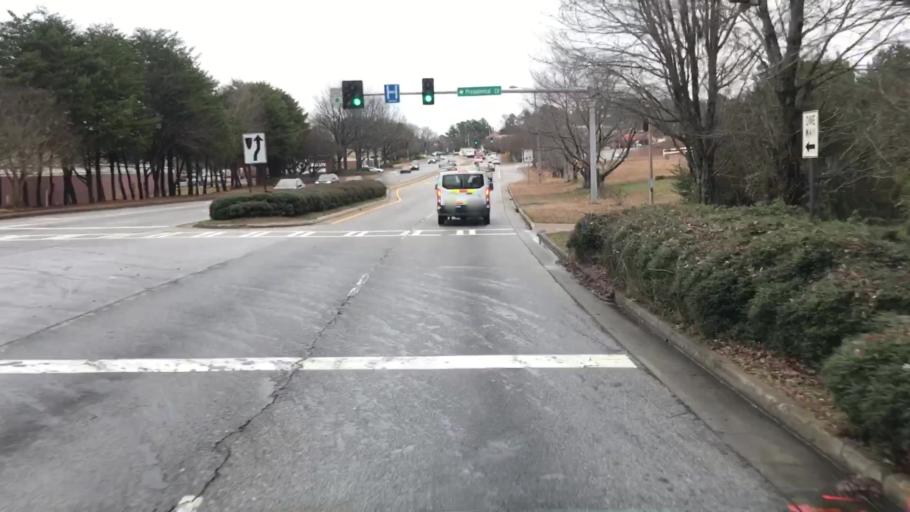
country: US
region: Georgia
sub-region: Gwinnett County
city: Snellville
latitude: 33.8743
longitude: -84.0181
